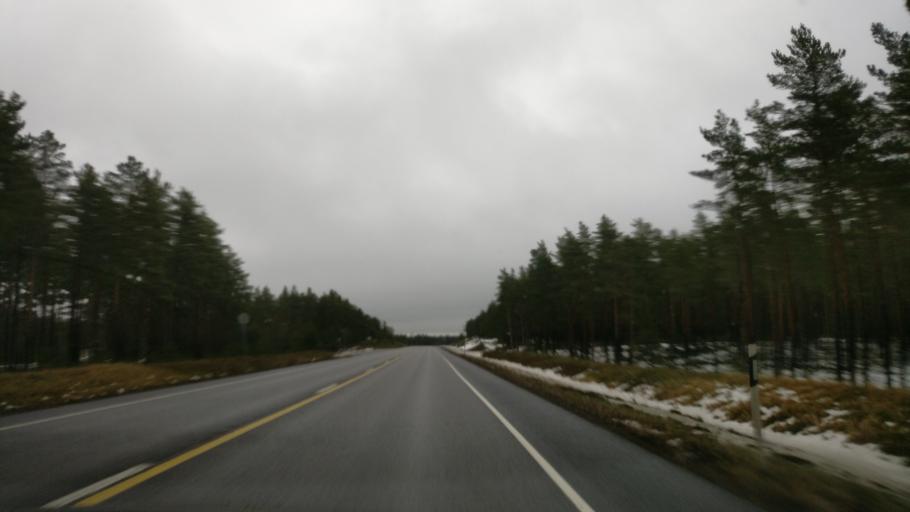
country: FI
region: Uusimaa
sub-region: Raaseporin
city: Hanko
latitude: 59.8944
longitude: 23.1829
